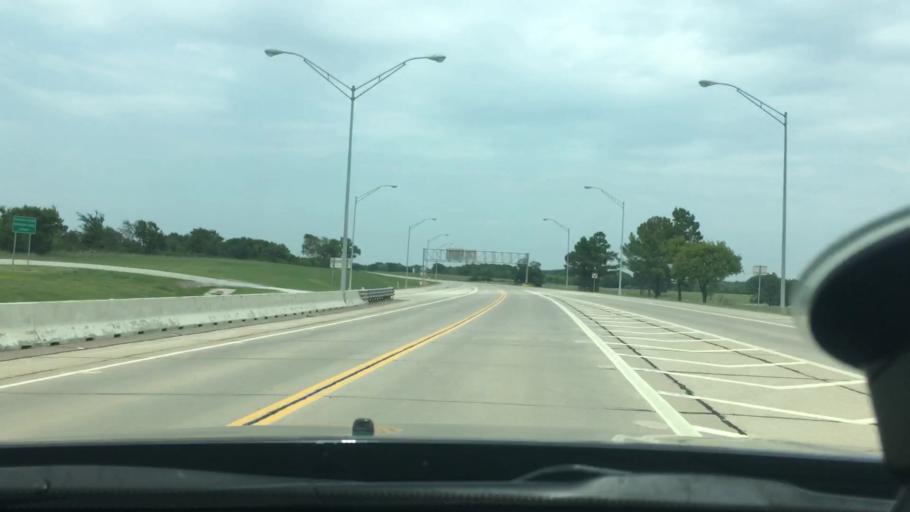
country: US
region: Oklahoma
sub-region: Murray County
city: Sulphur
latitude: 34.5672
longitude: -96.9294
